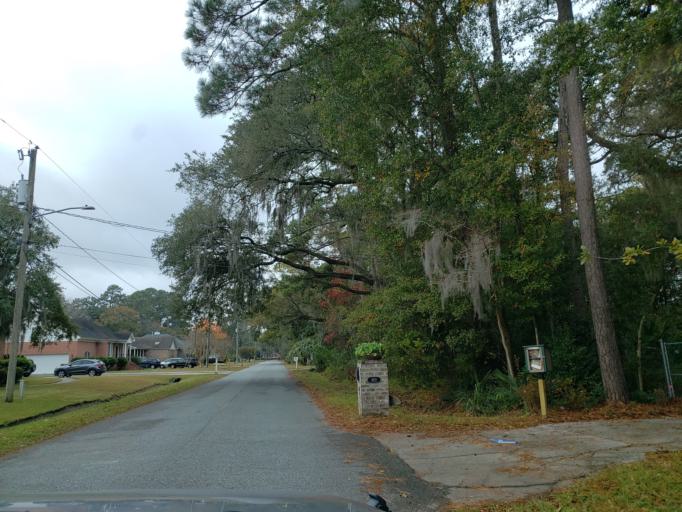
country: US
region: Georgia
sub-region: Chatham County
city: Wilmington Island
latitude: 32.0141
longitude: -80.9631
